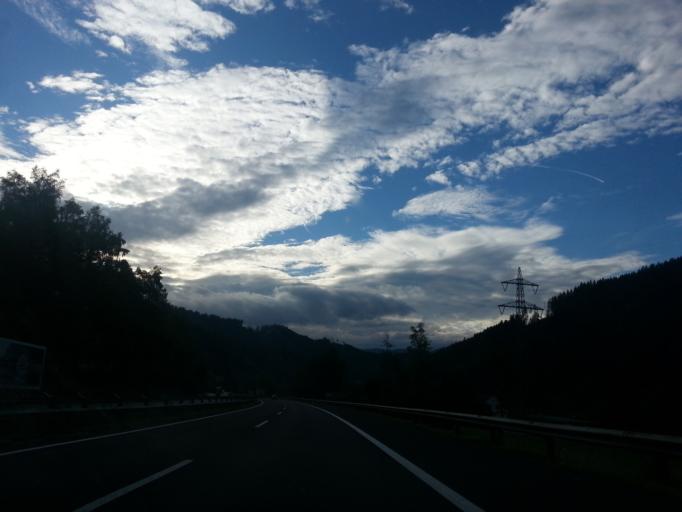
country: AT
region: Styria
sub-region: Politischer Bezirk Leoben
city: Sankt Michael in Obersteiermark
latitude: 47.3183
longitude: 15.0467
